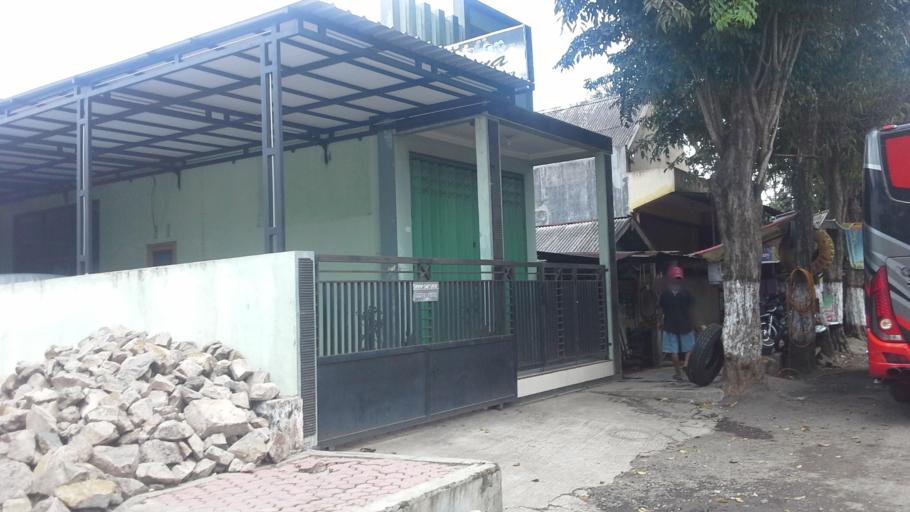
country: ID
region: East Java
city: Bondowoso
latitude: -7.9142
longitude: 113.8381
